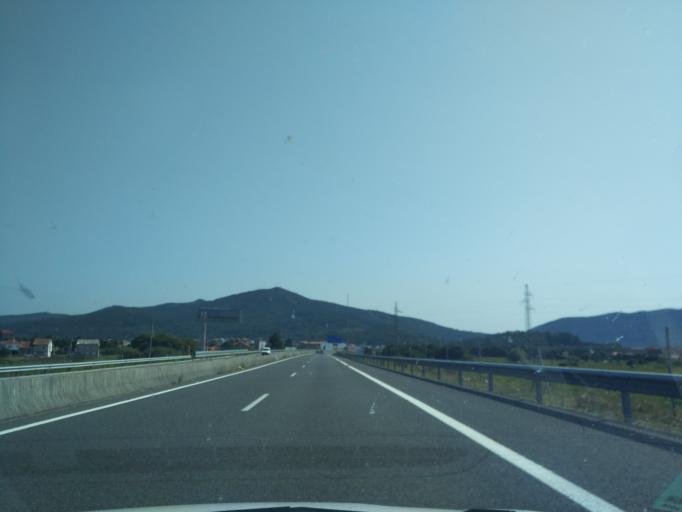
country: ES
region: Galicia
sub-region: Provincia da Coruna
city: Padron
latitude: 42.7276
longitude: -8.6701
